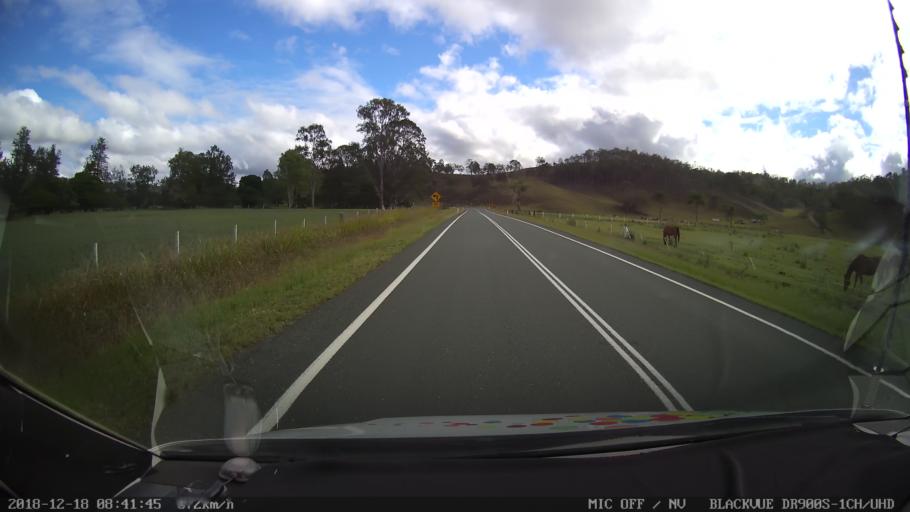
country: AU
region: Queensland
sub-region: Logan
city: Cedar Vale
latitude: -28.2333
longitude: 152.8594
